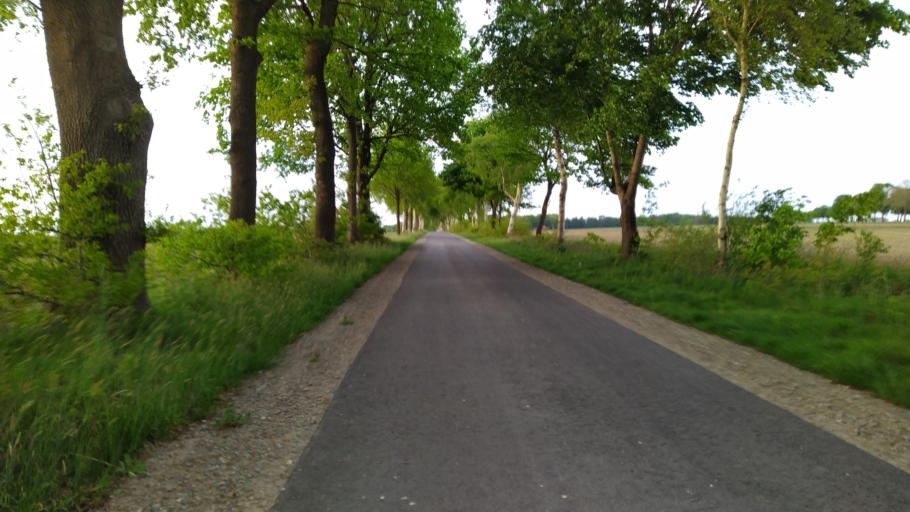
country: DE
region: Lower Saxony
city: Ahlerstedt
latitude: 53.4076
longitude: 9.4131
